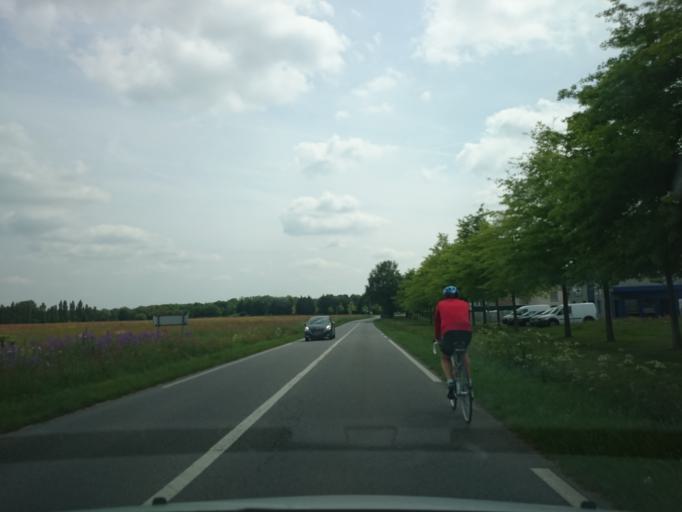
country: FR
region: Pays de la Loire
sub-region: Departement de la Loire-Atlantique
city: Pont-Saint-Martin
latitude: 47.1189
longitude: -1.5807
